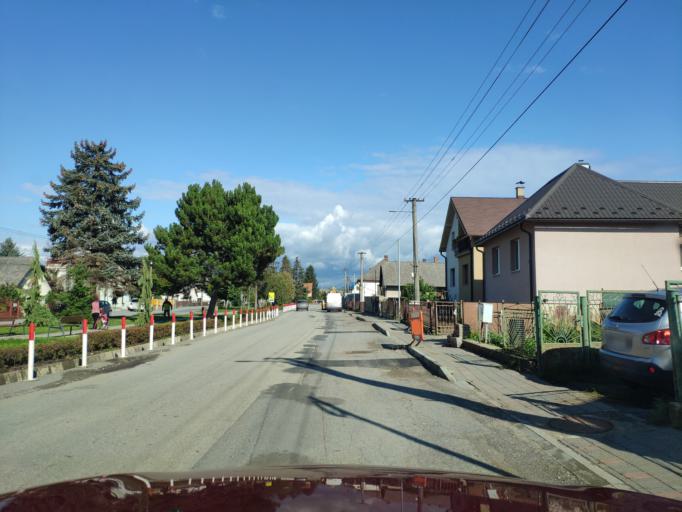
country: SK
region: Presovsky
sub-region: Okres Presov
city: Presov
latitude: 48.9198
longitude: 21.2604
